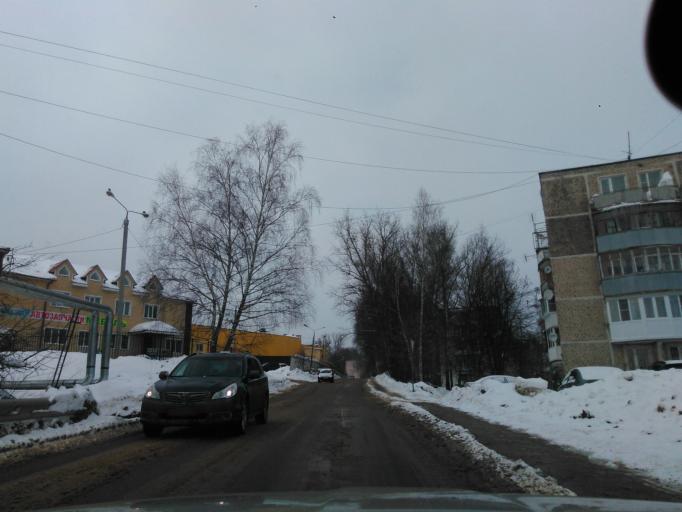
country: RU
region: Moskovskaya
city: Yakhroma
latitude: 56.2797
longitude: 37.4886
